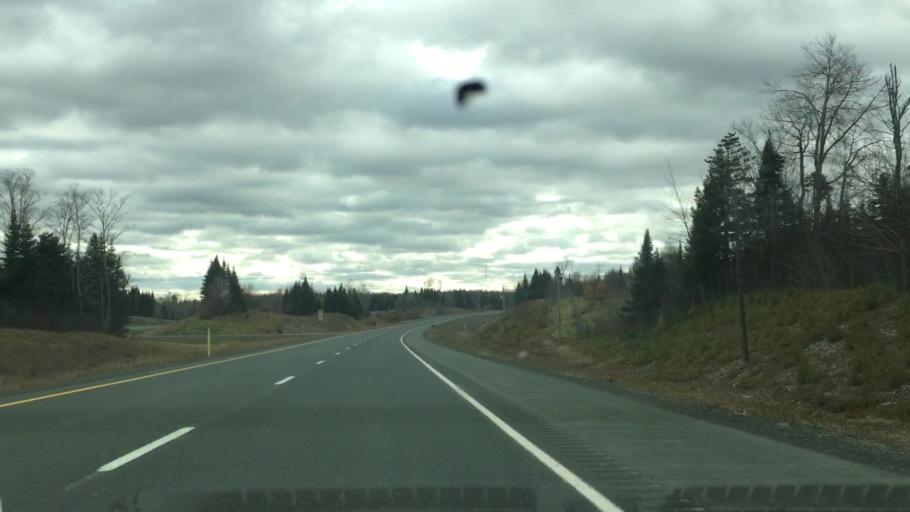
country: US
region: Maine
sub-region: Aroostook County
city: Easton
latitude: 46.6252
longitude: -67.7396
